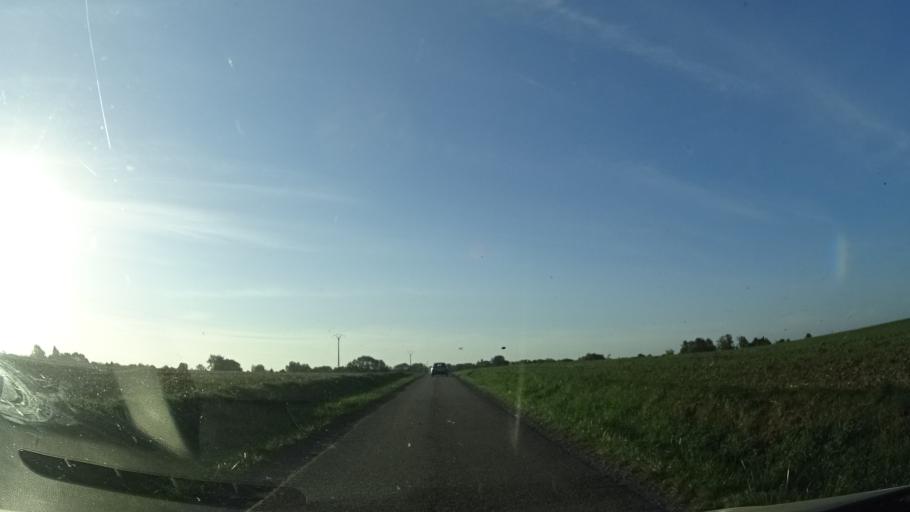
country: BE
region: Wallonia
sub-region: Province du Hainaut
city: Beaumont
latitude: 50.2540
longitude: 4.2533
